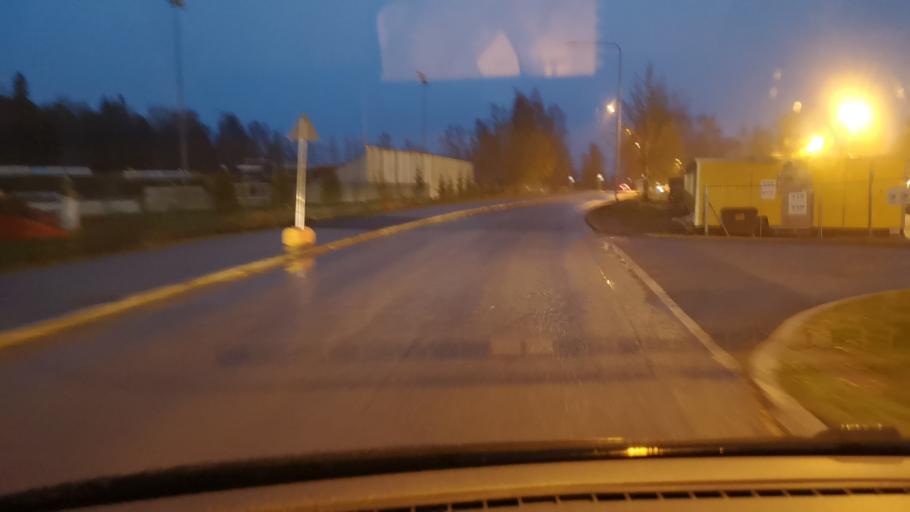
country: FI
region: Ostrobothnia
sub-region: Vaasa
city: Vaasa
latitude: 63.0854
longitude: 21.6199
